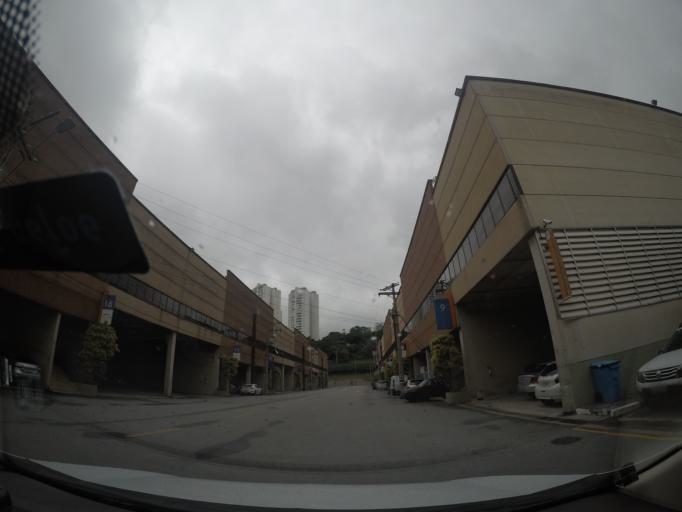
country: BR
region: Sao Paulo
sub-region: Osasco
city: Osasco
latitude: -23.4995
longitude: -46.7564
